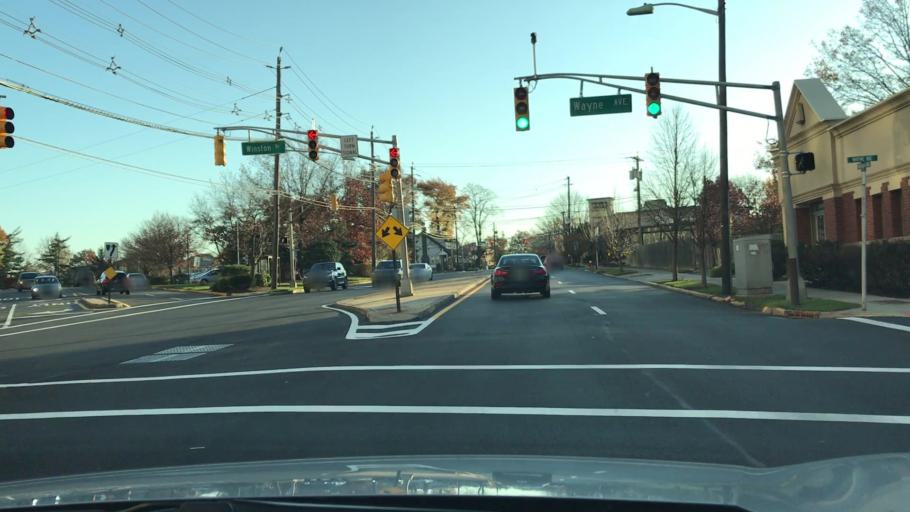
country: US
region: New Jersey
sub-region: Bergen County
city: Edgewater
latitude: 40.8286
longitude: -73.9805
